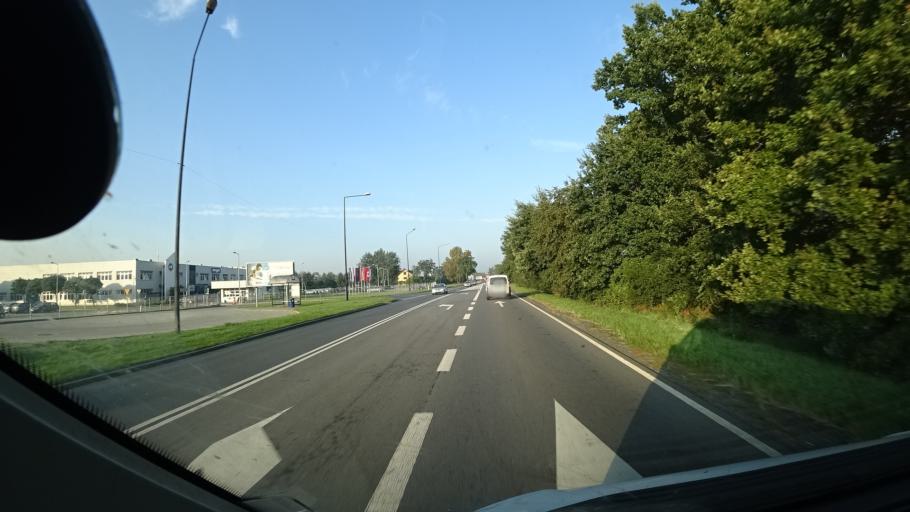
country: PL
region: Opole Voivodeship
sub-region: Powiat kedzierzynsko-kozielski
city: Kedzierzyn-Kozle
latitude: 50.3624
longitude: 18.2698
